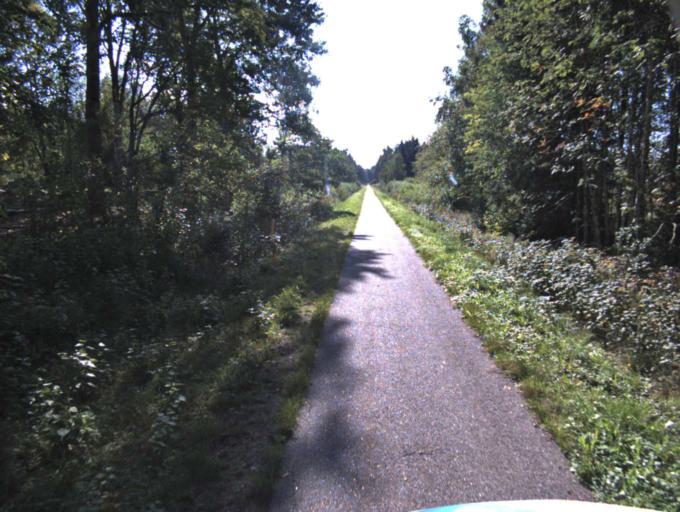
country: SE
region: Vaestra Goetaland
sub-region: Boras Kommun
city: Dalsjofors
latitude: 57.8320
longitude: 13.2192
